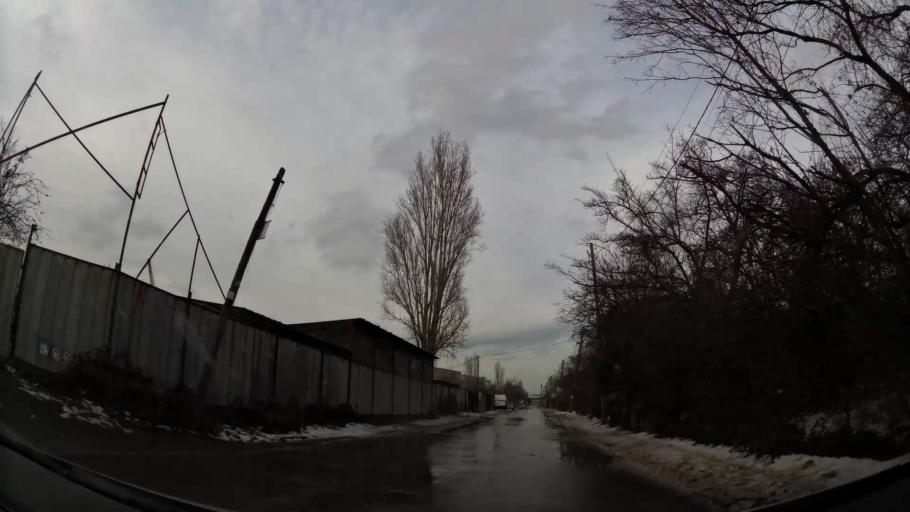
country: BG
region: Sofia-Capital
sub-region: Stolichna Obshtina
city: Sofia
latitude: 42.7229
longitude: 23.3295
